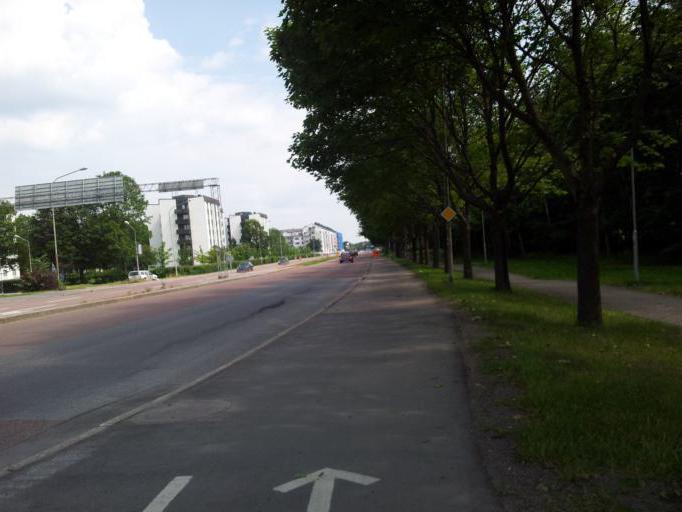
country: SE
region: Uppsala
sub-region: Uppsala Kommun
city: Uppsala
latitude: 59.8661
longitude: 17.6408
